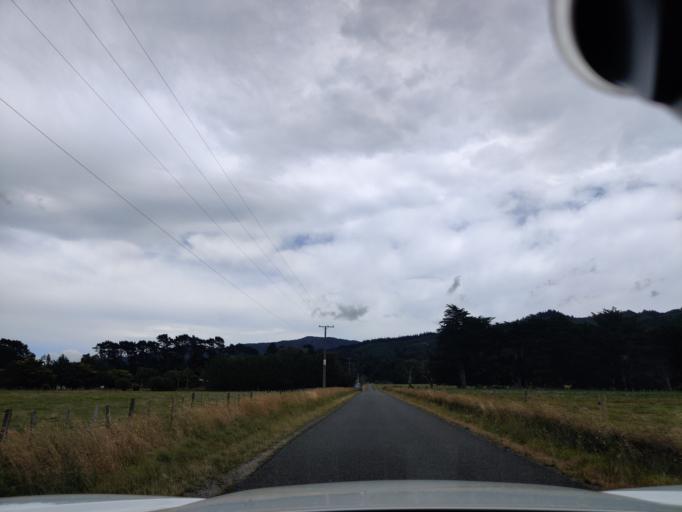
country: NZ
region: Wellington
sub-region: Masterton District
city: Masterton
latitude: -41.0367
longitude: 175.4315
